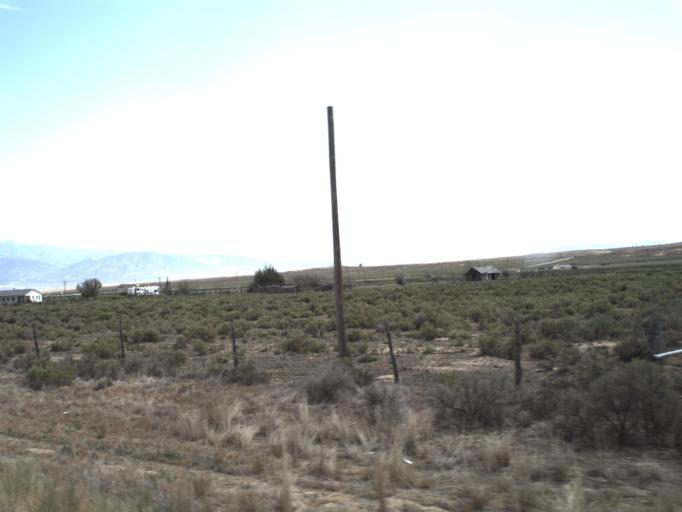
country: US
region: Utah
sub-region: Tooele County
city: Tooele
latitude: 40.1687
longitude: -112.4296
